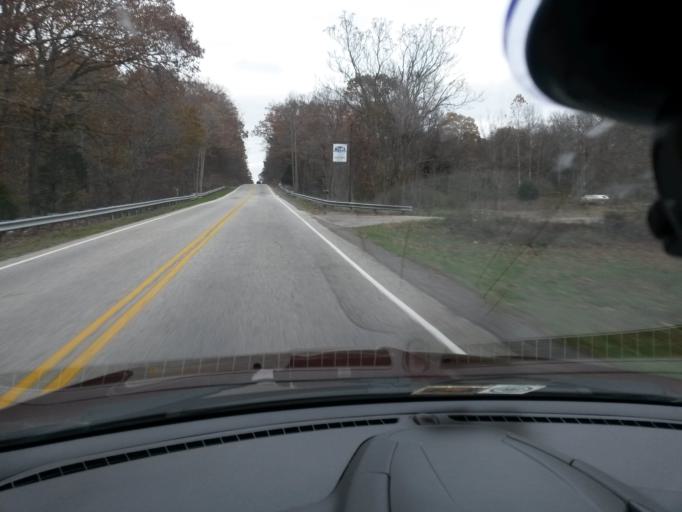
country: US
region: Virginia
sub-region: Rockbridge County
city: Glasgow
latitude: 37.6573
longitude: -79.4233
